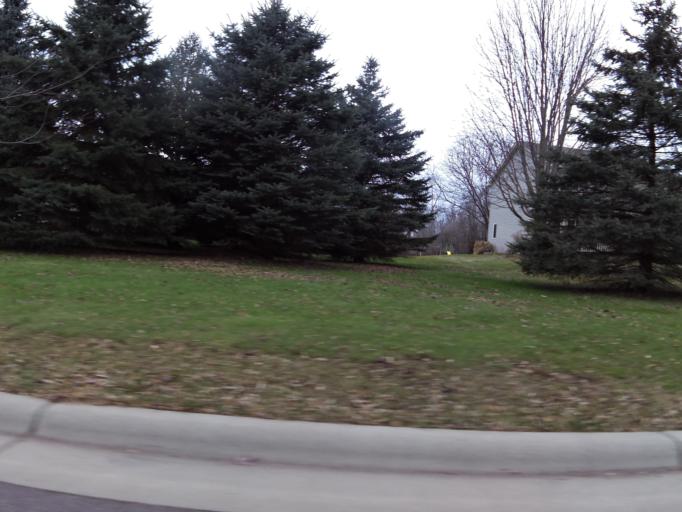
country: US
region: Minnesota
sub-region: Washington County
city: Lake Elmo
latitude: 44.9845
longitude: -92.8773
